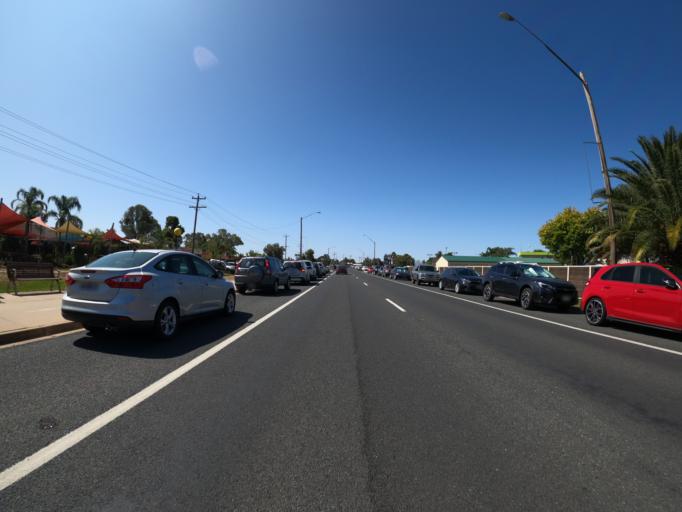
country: AU
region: New South Wales
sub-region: Corowa Shire
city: Mulwala
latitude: -35.9963
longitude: 146.0010
